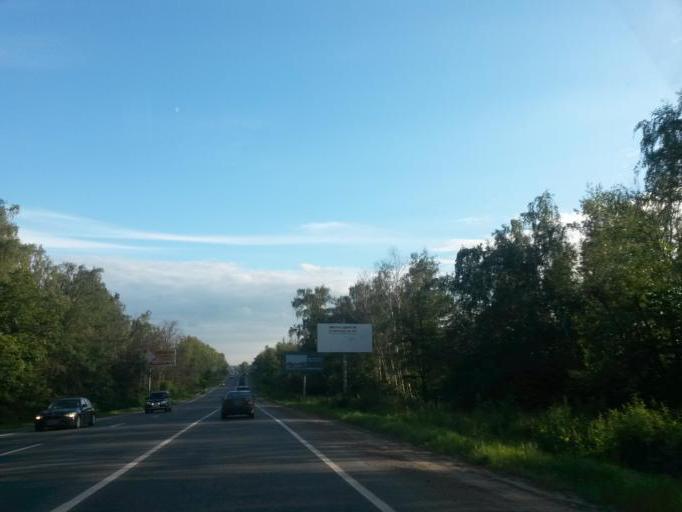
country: RU
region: Moskovskaya
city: Gorki-Leninskiye
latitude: 55.5245
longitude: 37.7650
